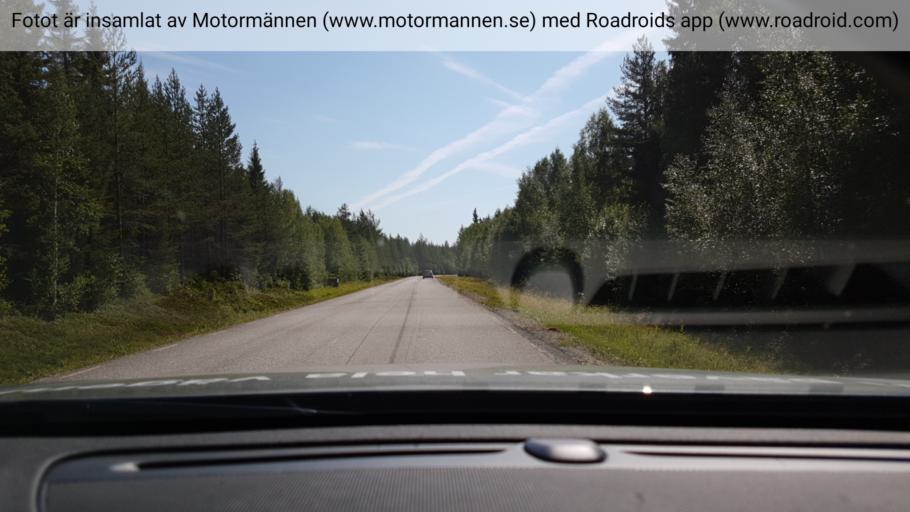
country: SE
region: Vaesterbotten
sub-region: Vannas Kommun
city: Vannasby
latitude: 64.0362
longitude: 19.9319
